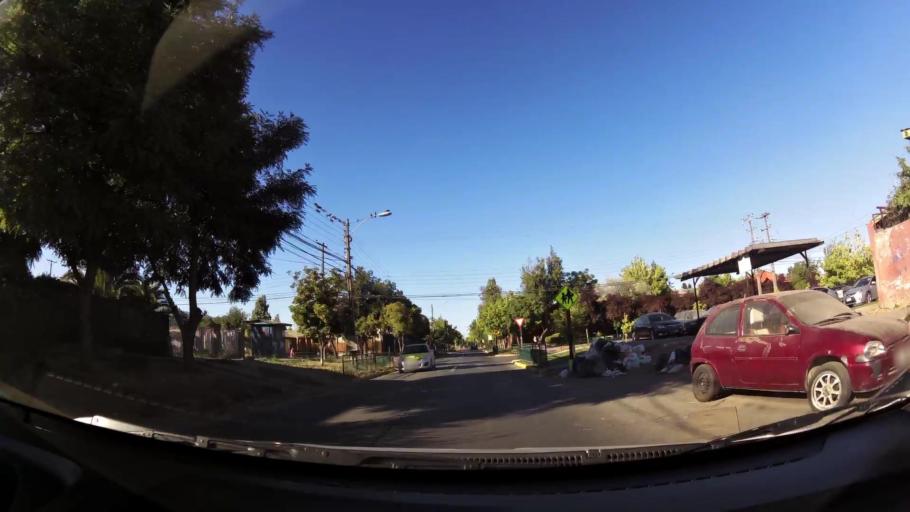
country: CL
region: O'Higgins
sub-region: Provincia de Cachapoal
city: Rancagua
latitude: -34.1752
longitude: -70.7221
